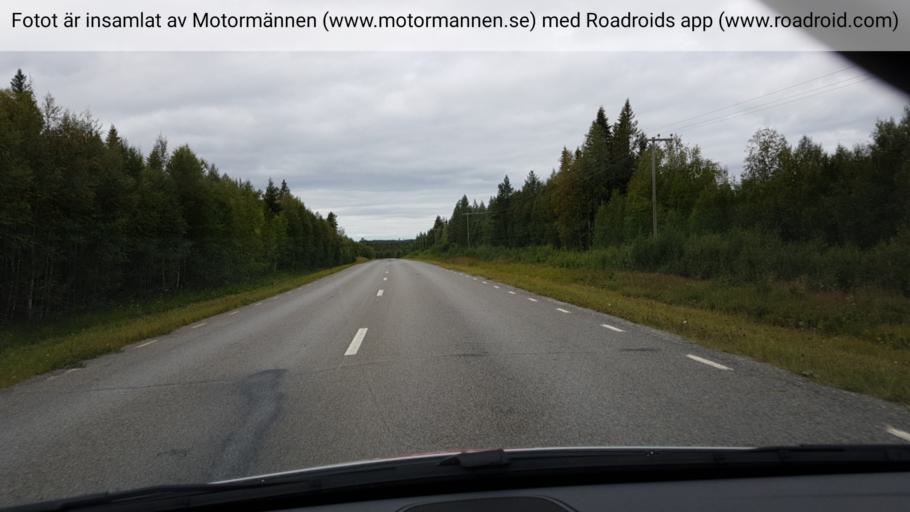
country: SE
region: Jaemtland
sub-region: Stroemsunds Kommun
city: Stroemsund
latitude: 64.3049
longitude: 15.2971
